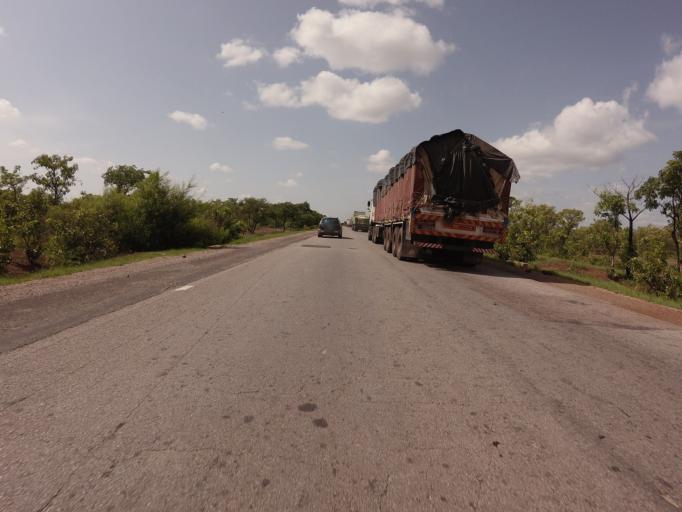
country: GH
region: Northern
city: Savelugu
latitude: 9.9540
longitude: -0.8352
